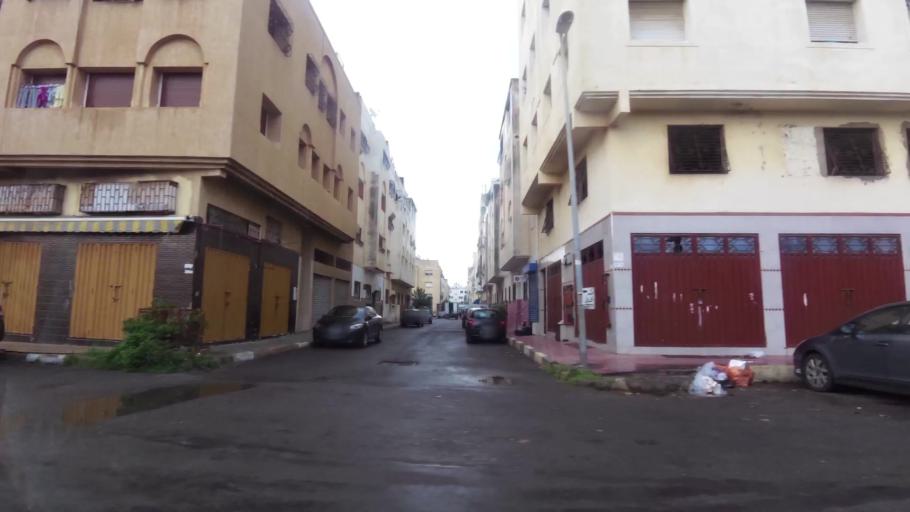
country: MA
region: Grand Casablanca
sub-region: Casablanca
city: Casablanca
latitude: 33.5394
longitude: -7.6864
